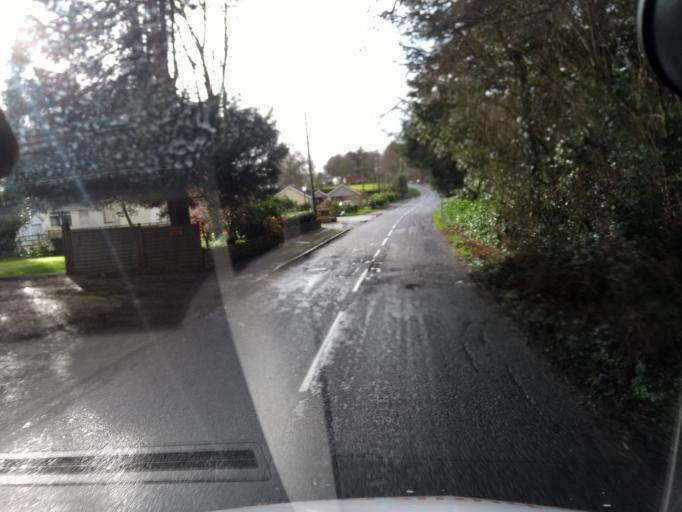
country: GB
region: England
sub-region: Somerset
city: Creech Saint Michael
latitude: 50.9762
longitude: -2.9979
